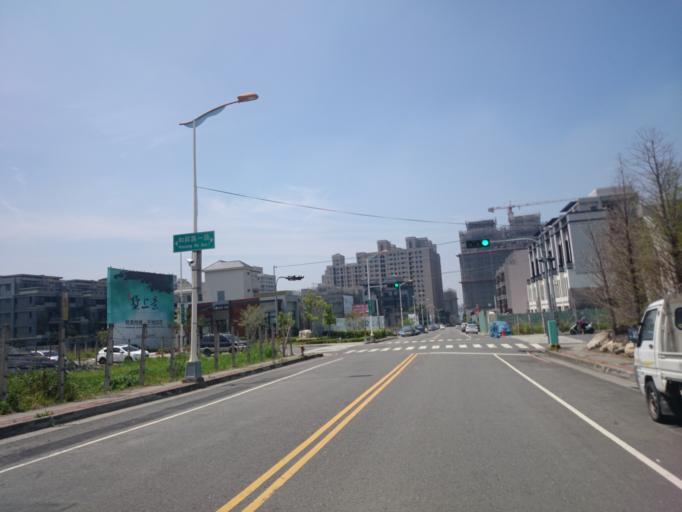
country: TW
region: Taiwan
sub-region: Taichung City
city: Taichung
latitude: 24.1754
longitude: 120.7277
